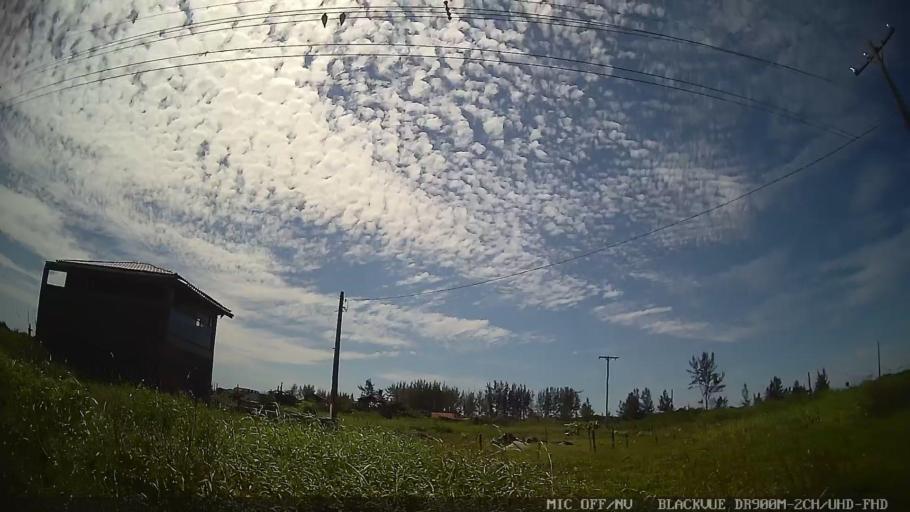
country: BR
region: Sao Paulo
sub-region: Iguape
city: Iguape
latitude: -24.8002
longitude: -47.6302
